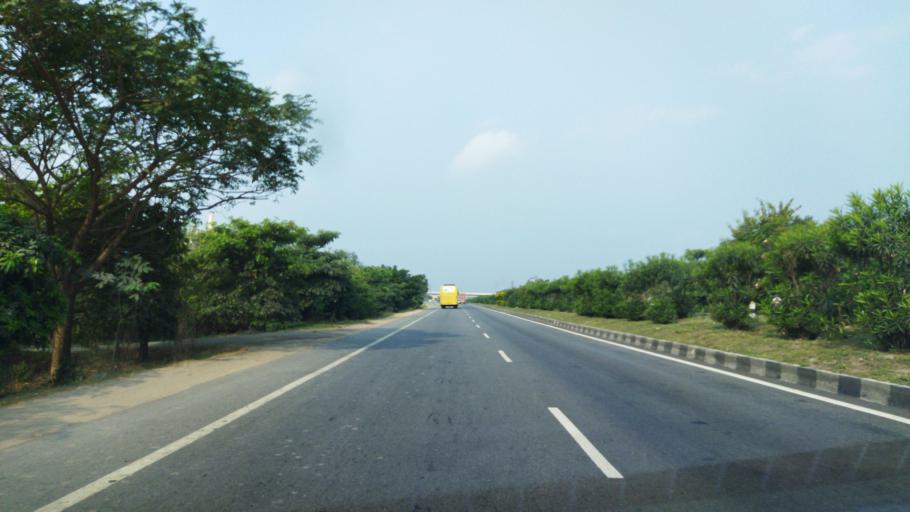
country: IN
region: Telangana
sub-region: Nalgonda
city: Nalgonda
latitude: 17.1681
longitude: 79.4003
